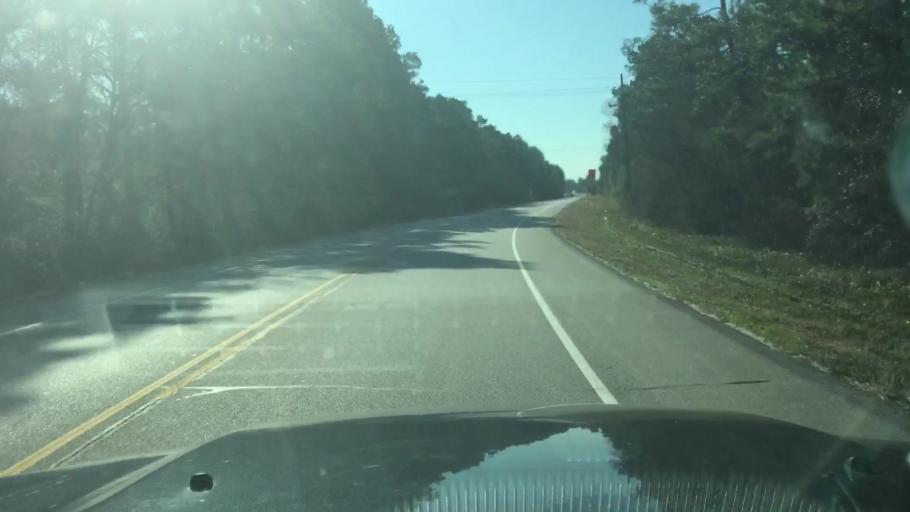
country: US
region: Texas
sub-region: Montgomery County
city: Porter Heights
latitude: 30.2237
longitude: -95.3609
